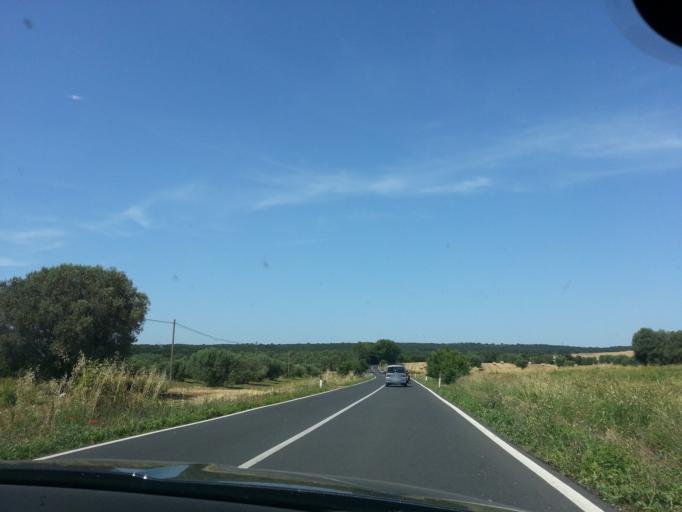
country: IT
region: Latium
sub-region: Provincia di Viterbo
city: Monte Romano
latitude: 42.2632
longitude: 11.8606
